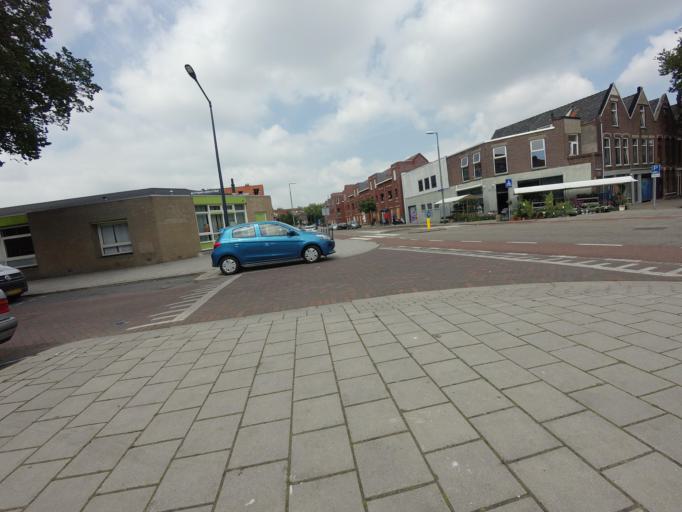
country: NL
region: South Holland
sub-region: Gemeente Schiedam
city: Schiedam
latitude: 51.9135
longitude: 4.3886
